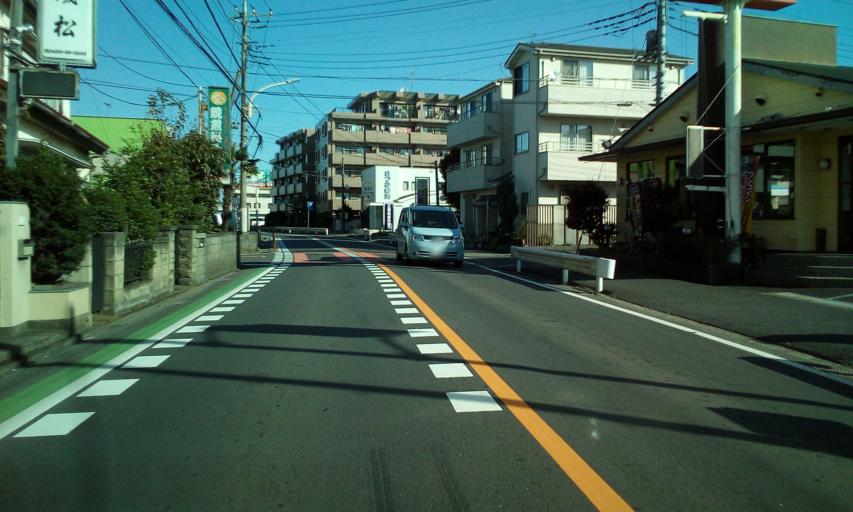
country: JP
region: Chiba
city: Nagareyama
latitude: 35.8510
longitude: 139.8820
